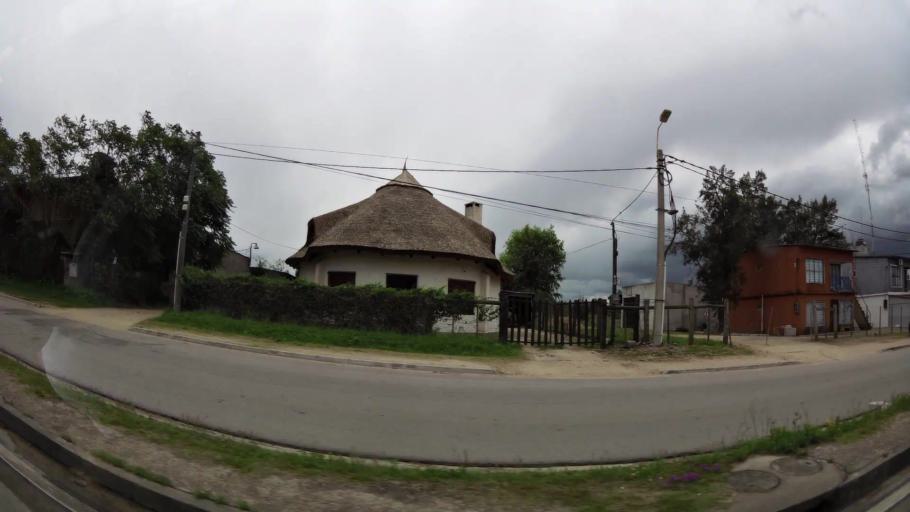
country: UY
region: Canelones
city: Toledo
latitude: -34.7958
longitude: -56.1393
